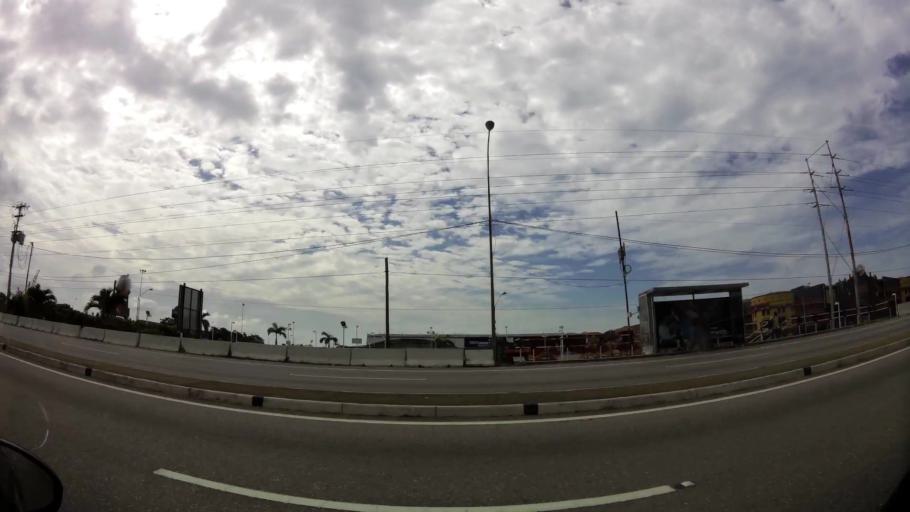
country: TT
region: City of Port of Spain
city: Mucurapo
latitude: 10.6598
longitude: -61.5322
